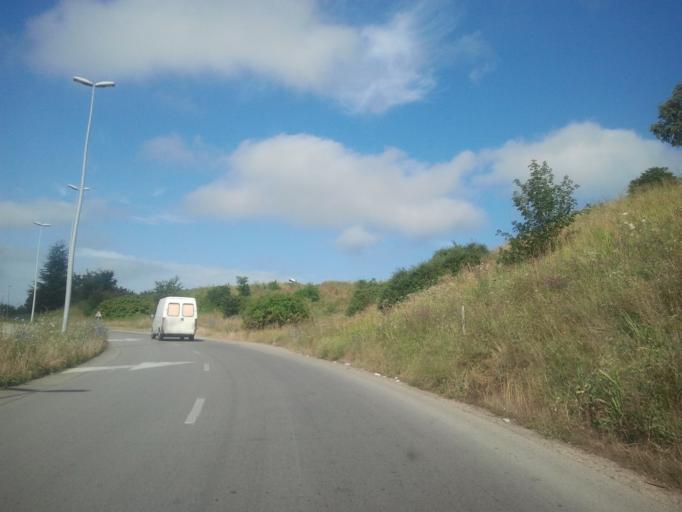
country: RS
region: Autonomna Pokrajina Vojvodina
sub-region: Juznobacki Okrug
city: Petrovaradin
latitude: 45.2257
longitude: 19.8739
